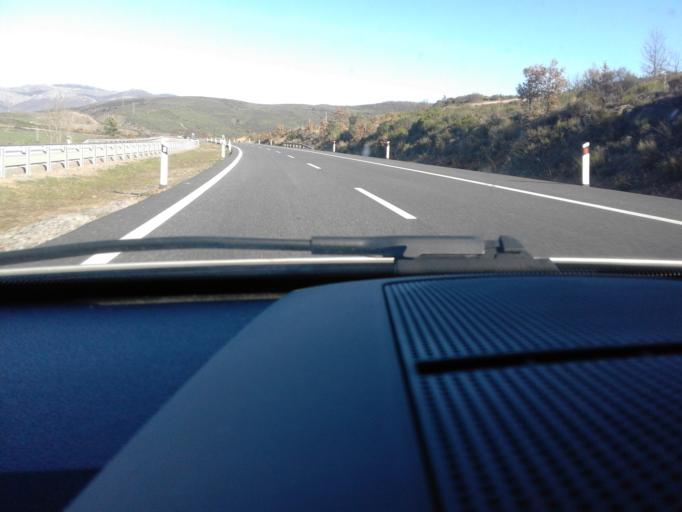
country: ES
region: Castille and Leon
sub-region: Provincia de Leon
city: Santa Maria de Ordas
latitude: 42.7416
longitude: -5.7755
